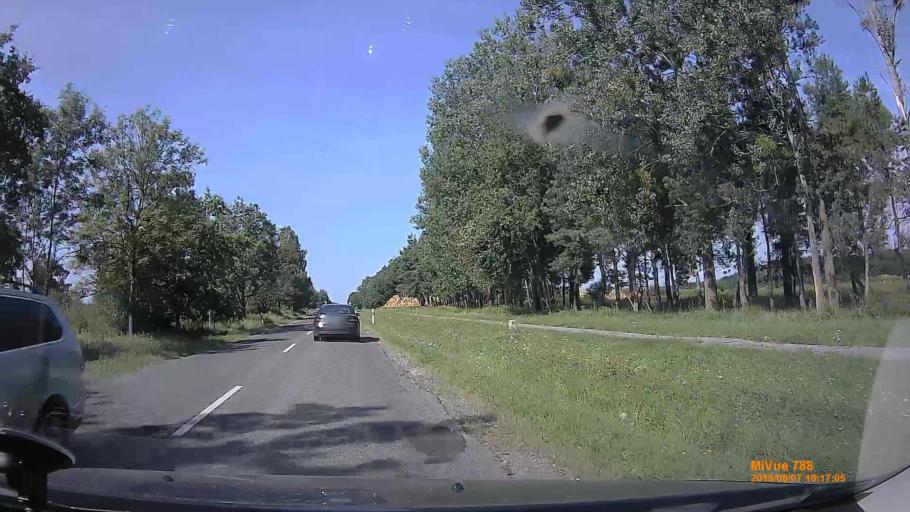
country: HU
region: Zala
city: Lenti
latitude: 46.6360
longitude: 16.5847
